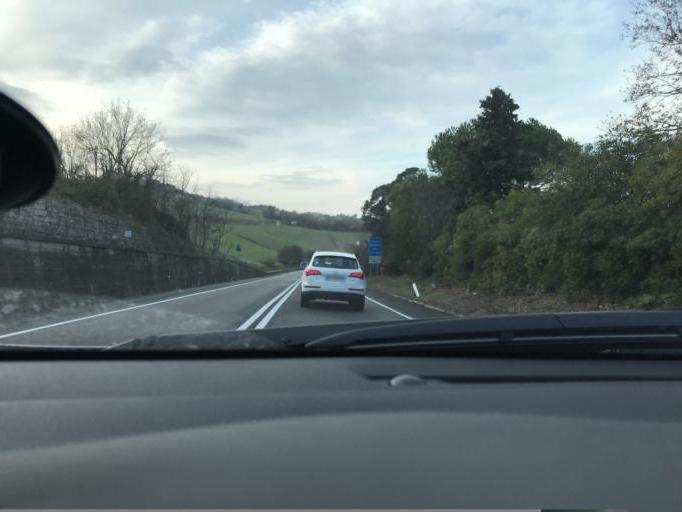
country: IT
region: The Marches
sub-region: Provincia di Ancona
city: Falconara Marittima
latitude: 43.6017
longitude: 13.4302
